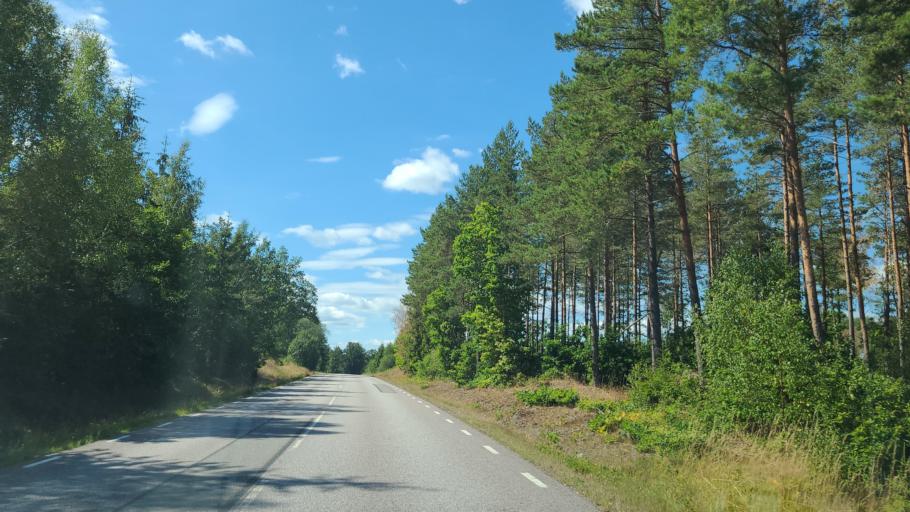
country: SE
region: Kalmar
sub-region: Emmaboda Kommun
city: Emmaboda
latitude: 56.5376
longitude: 15.6626
